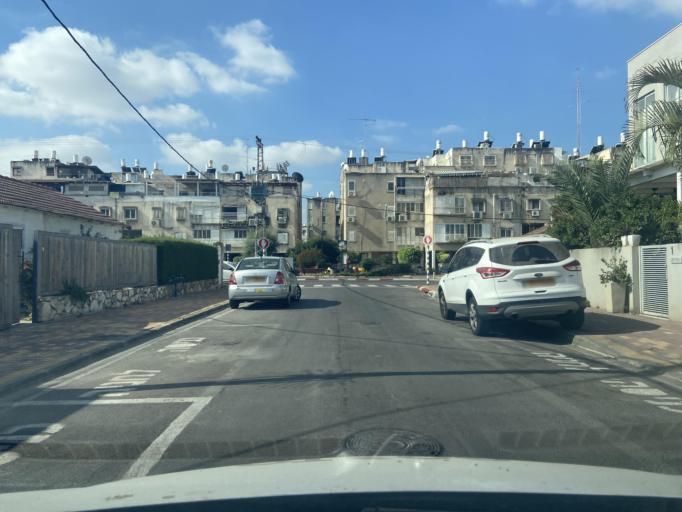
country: IL
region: Central District
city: Yehud
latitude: 32.0317
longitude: 34.8961
